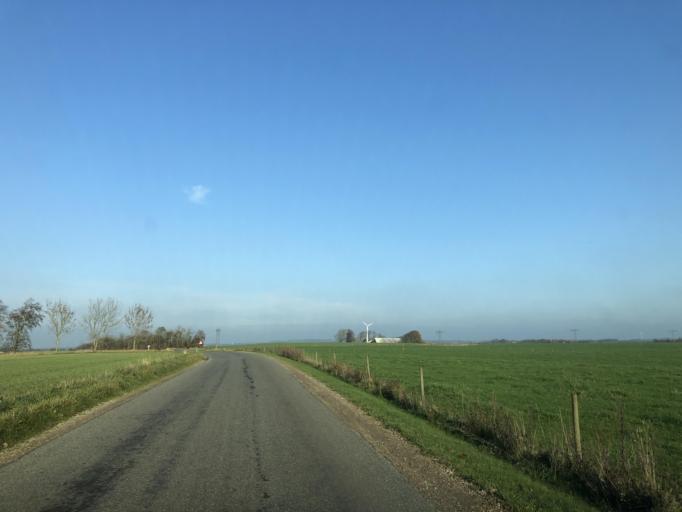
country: DK
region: Central Jutland
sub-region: Holstebro Kommune
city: Vinderup
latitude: 56.3901
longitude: 8.7313
